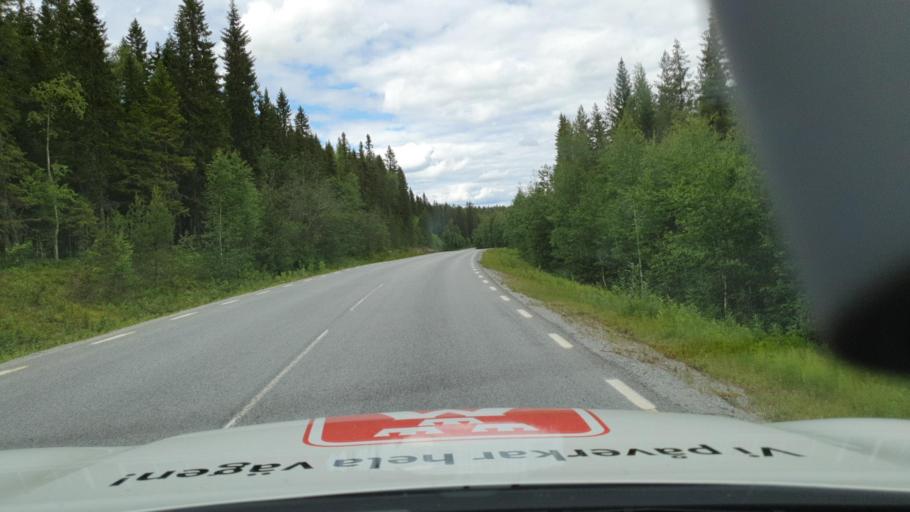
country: SE
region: Vaesterbotten
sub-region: Bjurholms Kommun
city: Bjurholm
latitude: 63.8856
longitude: 19.0629
